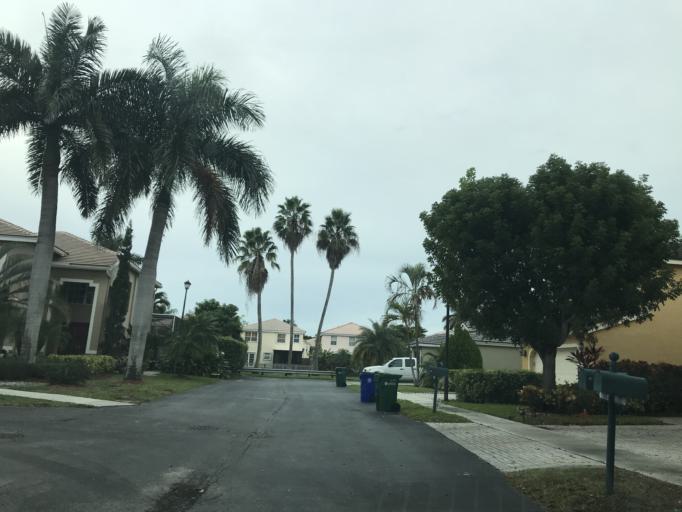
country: US
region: Florida
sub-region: Broward County
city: Margate
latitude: 26.2660
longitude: -80.2051
